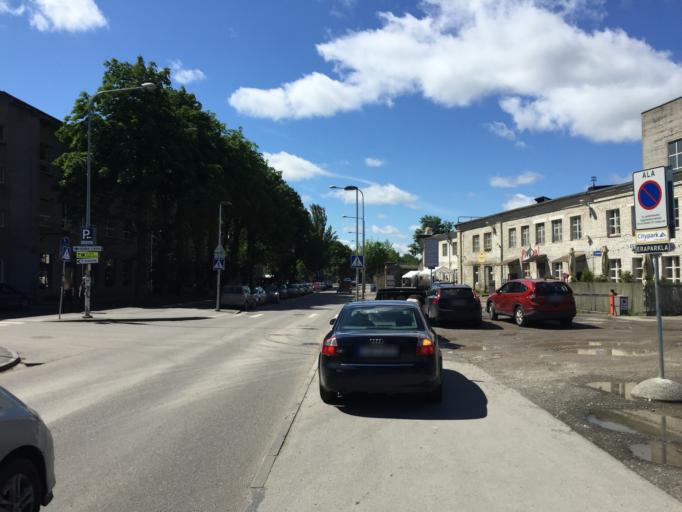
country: EE
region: Harju
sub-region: Tallinna linn
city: Tallinn
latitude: 59.4405
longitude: 24.7294
